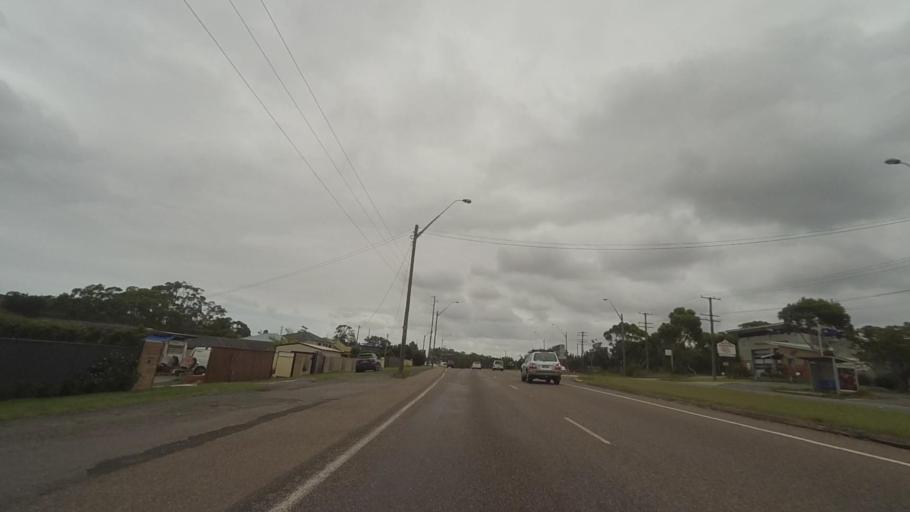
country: AU
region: New South Wales
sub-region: Wyong Shire
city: Buff Point
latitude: -33.1982
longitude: 151.5240
